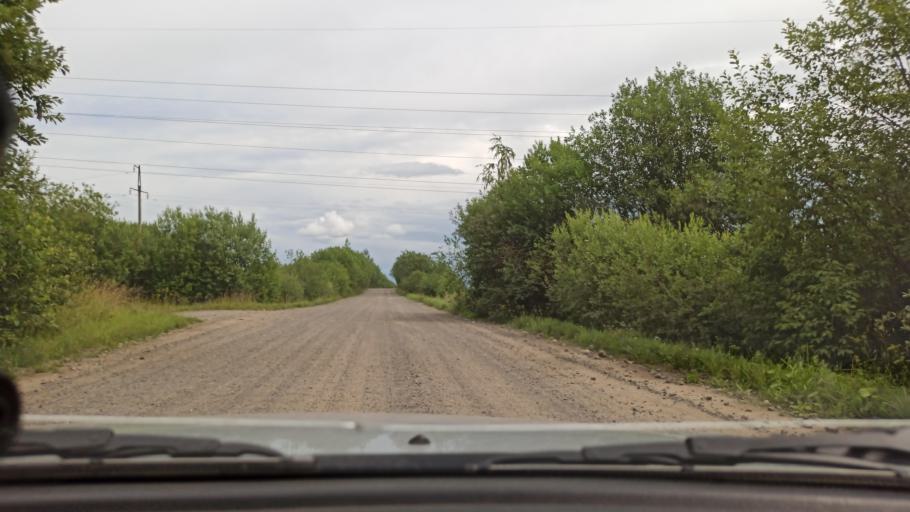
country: RU
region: Vologda
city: Molochnoye
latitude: 59.3695
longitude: 39.6830
